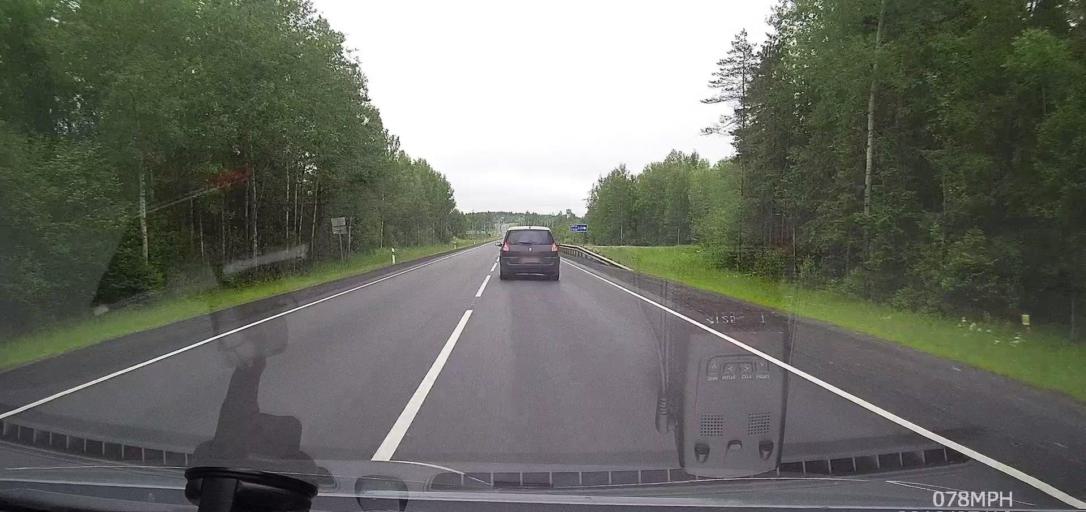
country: RU
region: Leningrad
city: Syas'stroy
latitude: 60.2654
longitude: 32.7821
